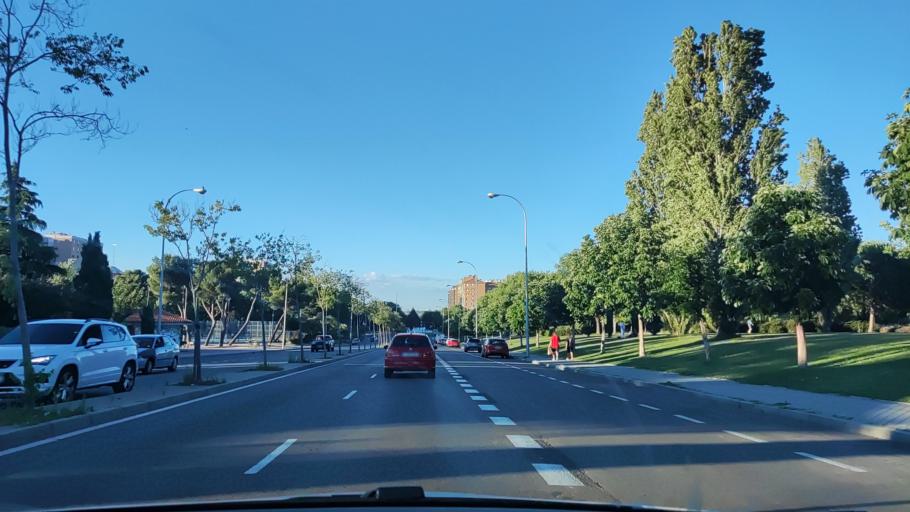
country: ES
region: Madrid
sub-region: Provincia de Madrid
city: Latina
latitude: 40.3715
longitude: -3.7365
